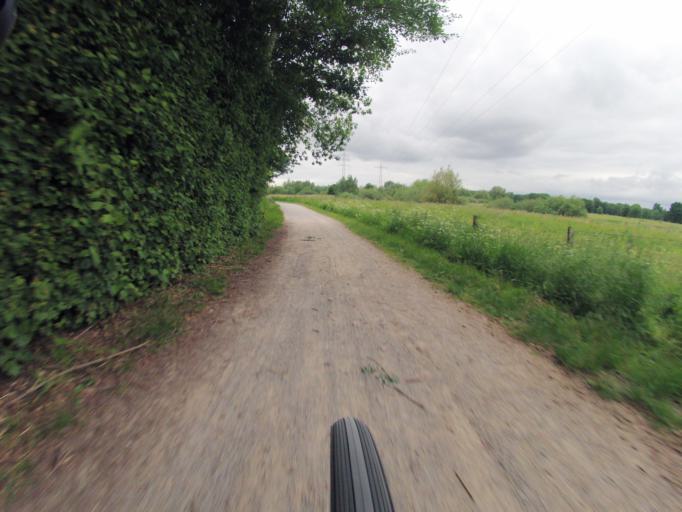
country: DE
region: North Rhine-Westphalia
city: Emsdetten
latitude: 52.1785
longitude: 7.5461
